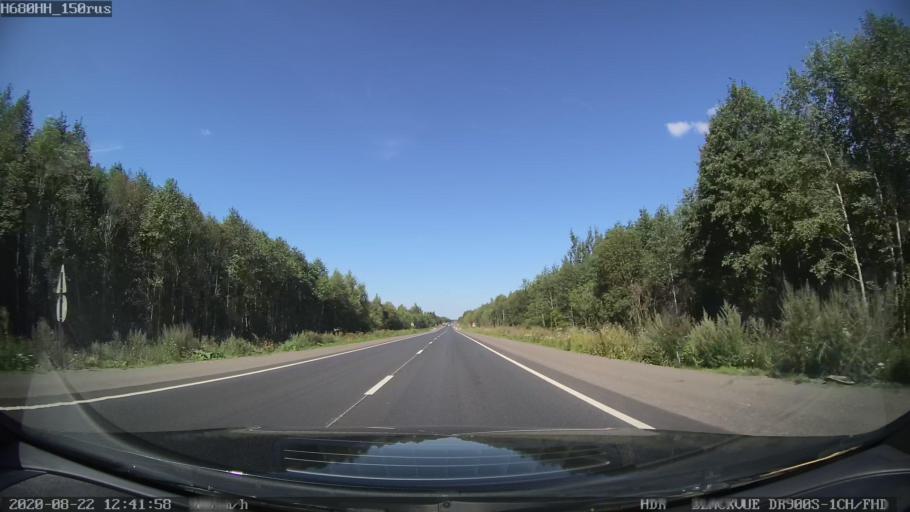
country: RU
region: Tverskaya
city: Rameshki
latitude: 57.3548
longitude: 36.0977
